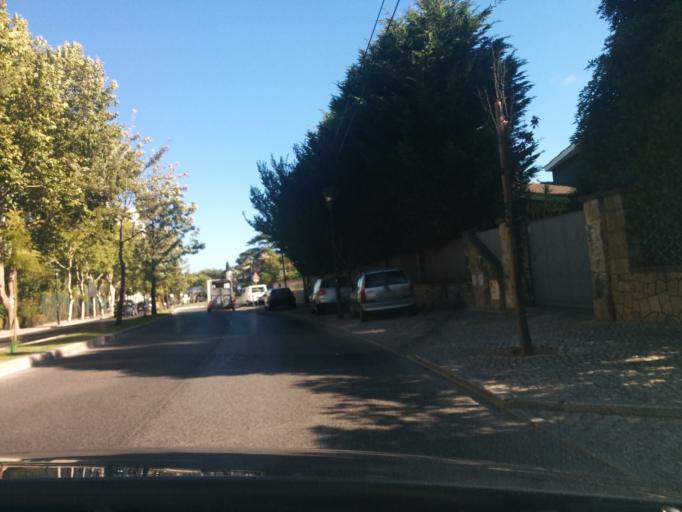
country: PT
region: Lisbon
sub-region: Cascais
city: Cascais
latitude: 38.7026
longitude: -9.4346
